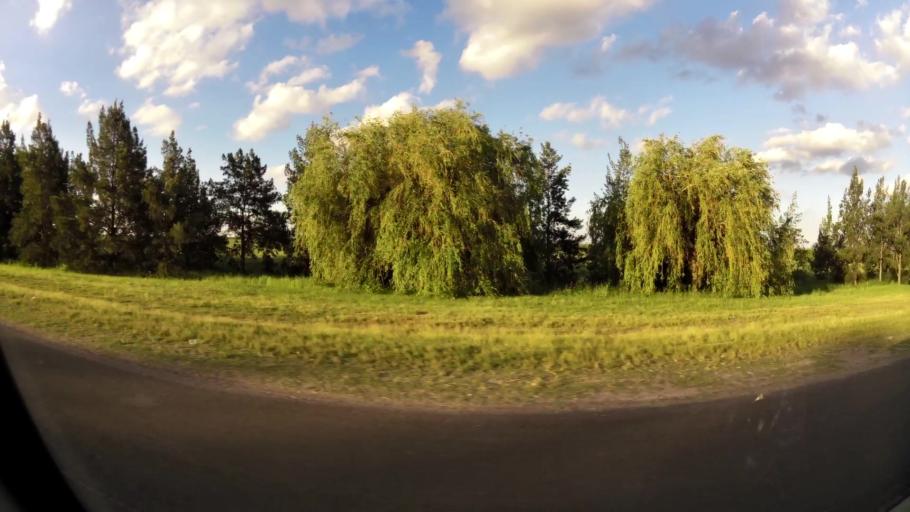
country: AR
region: Buenos Aires
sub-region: Partido de La Plata
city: La Plata
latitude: -34.8704
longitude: -57.9882
